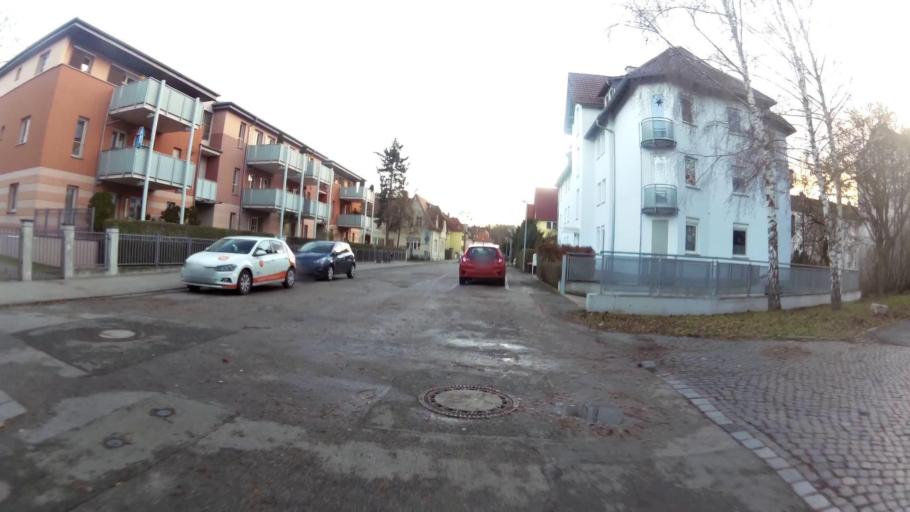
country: DE
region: Thuringia
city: Weimar
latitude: 50.9787
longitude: 11.3139
